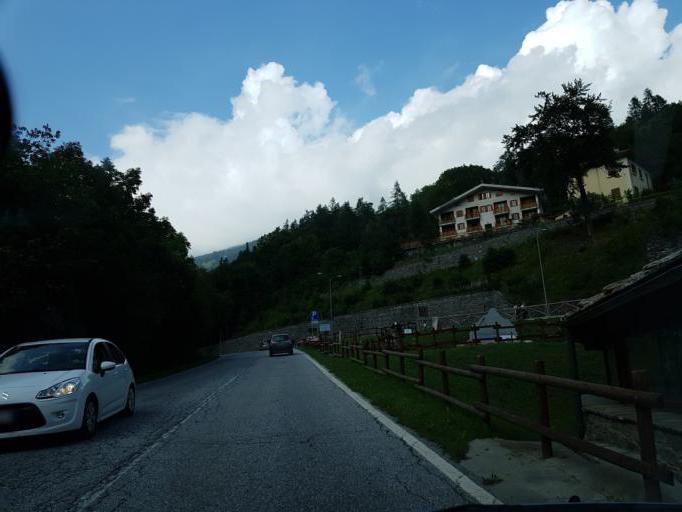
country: IT
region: Piedmont
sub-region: Provincia di Cuneo
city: Casteldelfino
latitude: 44.5916
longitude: 7.0677
